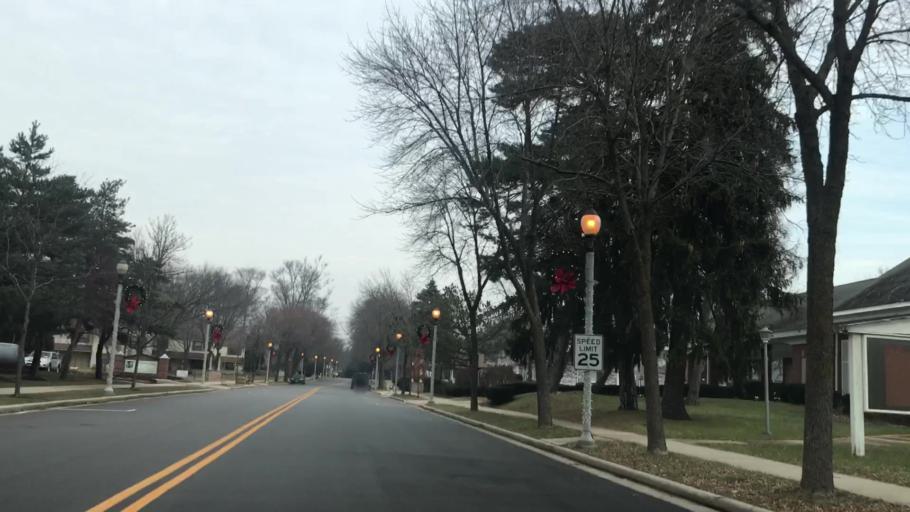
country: US
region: Wisconsin
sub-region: Ozaukee County
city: Mequon
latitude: 43.2337
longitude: -87.9817
